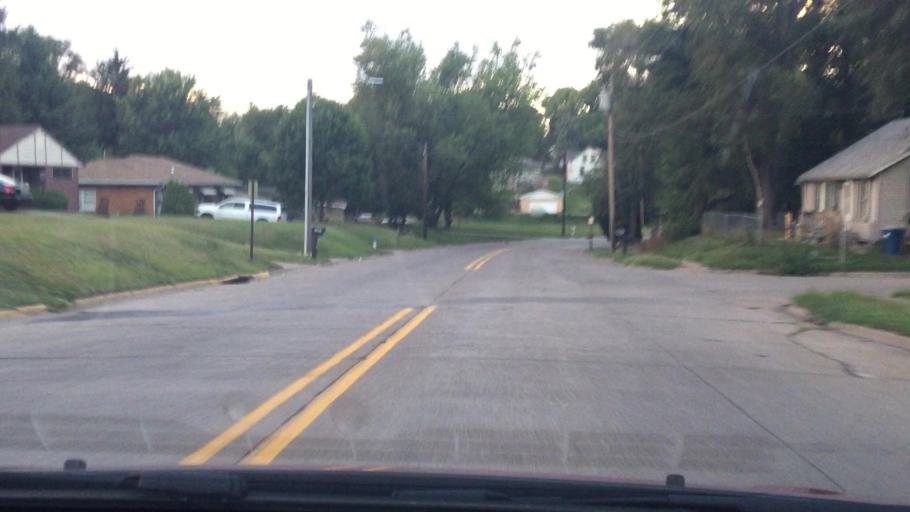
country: US
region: Iowa
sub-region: Muscatine County
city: Muscatine
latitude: 41.4201
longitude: -91.0594
